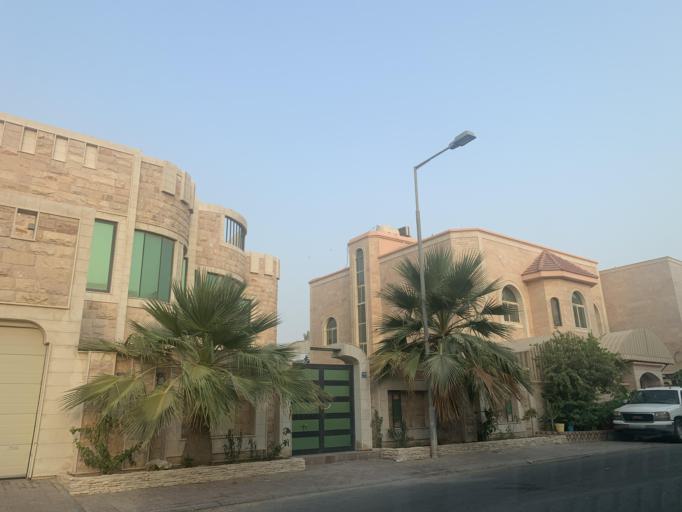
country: BH
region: Manama
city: Jidd Hafs
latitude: 26.2244
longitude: 50.5150
